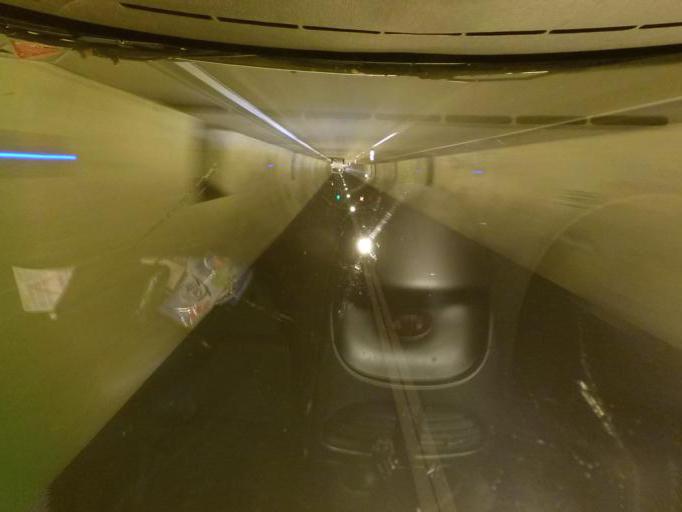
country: CZ
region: Ustecky
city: Libouchec
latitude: 50.7530
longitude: 13.9893
